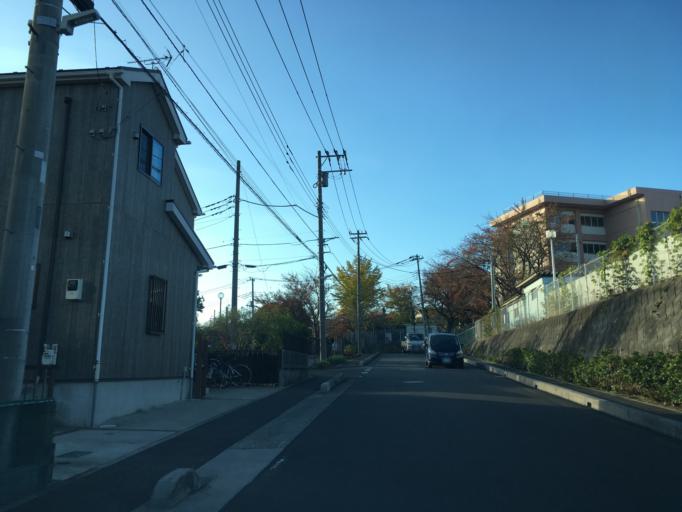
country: JP
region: Saitama
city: Tokorozawa
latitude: 35.7846
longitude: 139.4320
